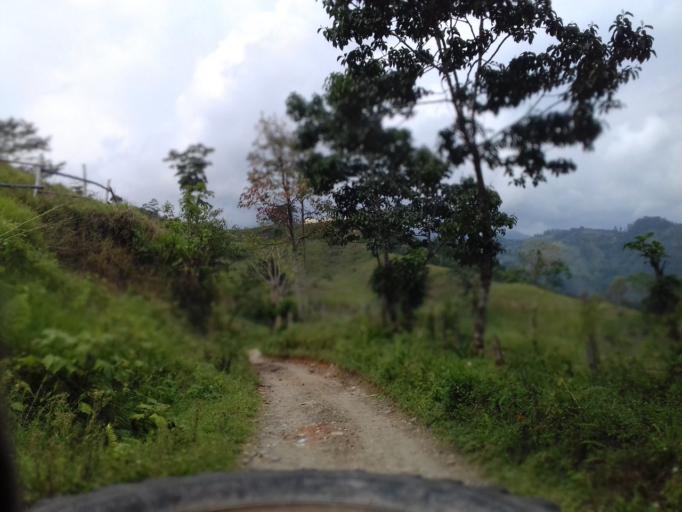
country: CO
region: Tolima
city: Libano
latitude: 4.9284
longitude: -75.0874
